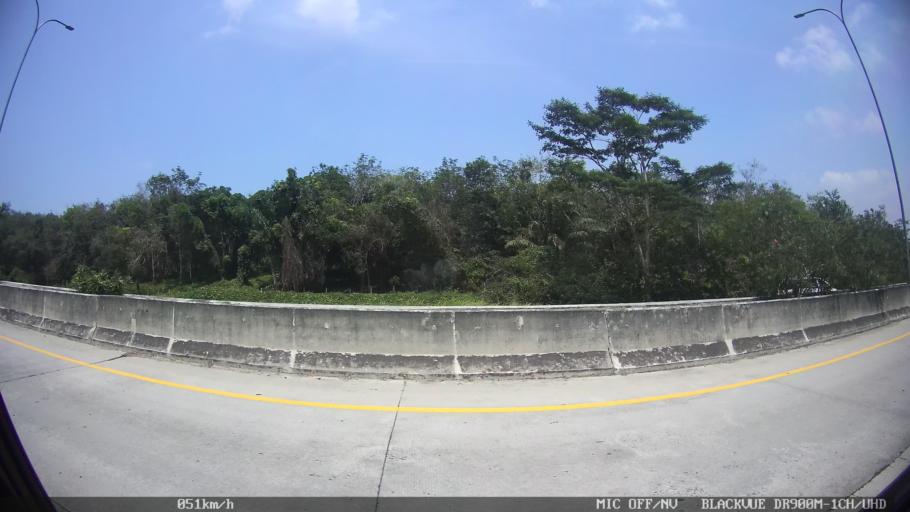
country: ID
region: Lampung
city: Kedaton
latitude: -5.3697
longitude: 105.3267
